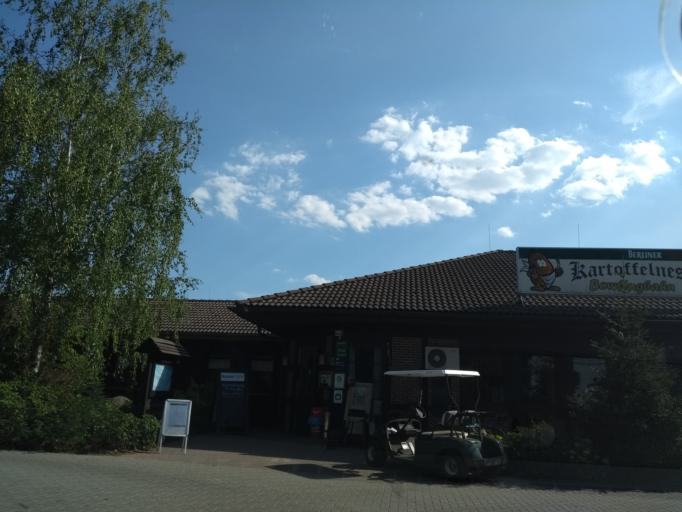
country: DE
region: Brandenburg
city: Luebben
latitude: 51.8579
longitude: 13.8568
